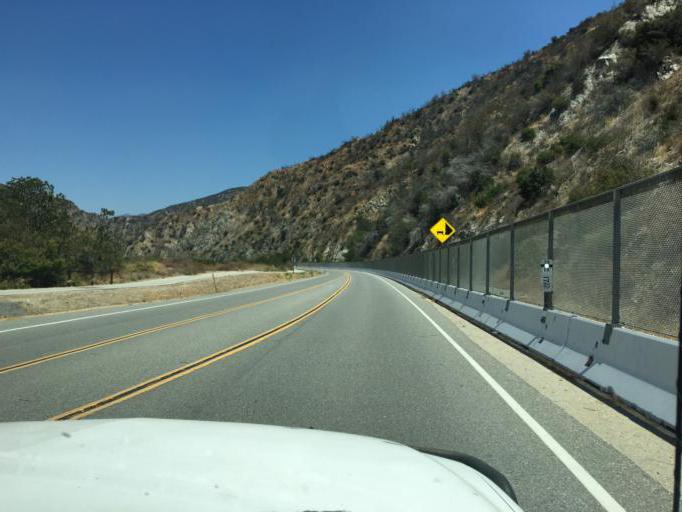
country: US
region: California
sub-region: Los Angeles County
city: Azusa
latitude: 34.1586
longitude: -117.9029
